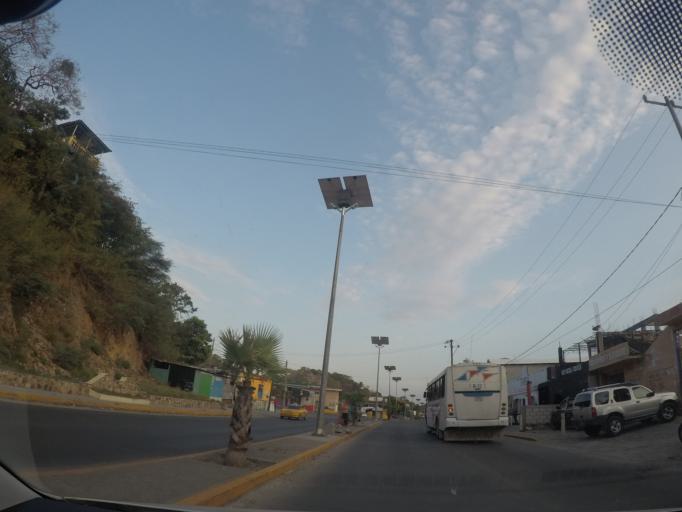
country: MX
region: Oaxaca
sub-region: Salina Cruz
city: Salina Cruz
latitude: 16.1940
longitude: -95.2016
